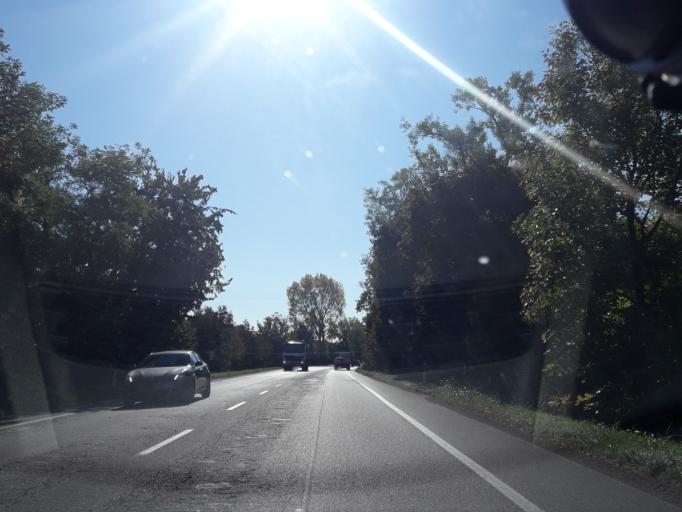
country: IT
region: Friuli Venezia Giulia
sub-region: Provincia di Udine
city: Povoletto
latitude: 46.1091
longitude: 13.2814
